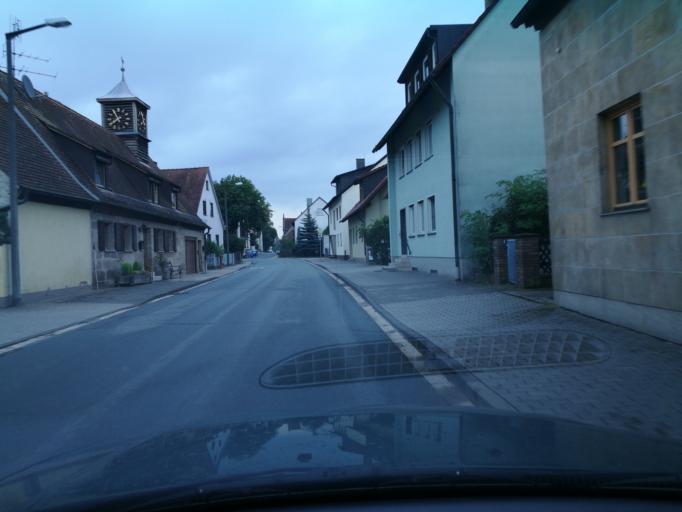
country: DE
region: Bavaria
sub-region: Regierungsbezirk Mittelfranken
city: Obermichelbach
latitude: 49.5404
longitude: 10.9604
